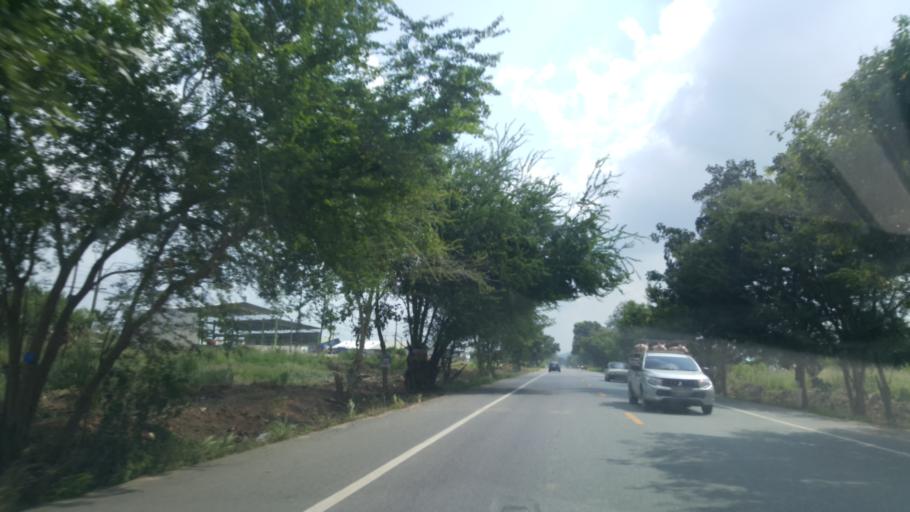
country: TH
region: Chon Buri
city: Sattahip
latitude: 12.7266
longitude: 100.9659
